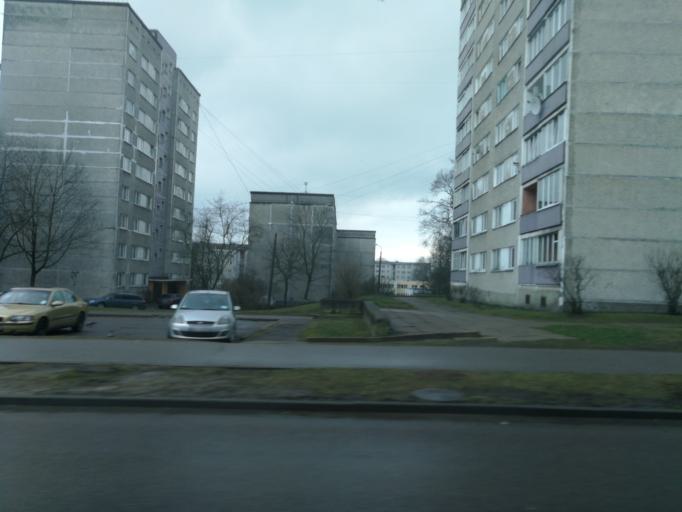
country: LV
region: Riga
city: Bolderaja
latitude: 57.0324
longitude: 24.1084
